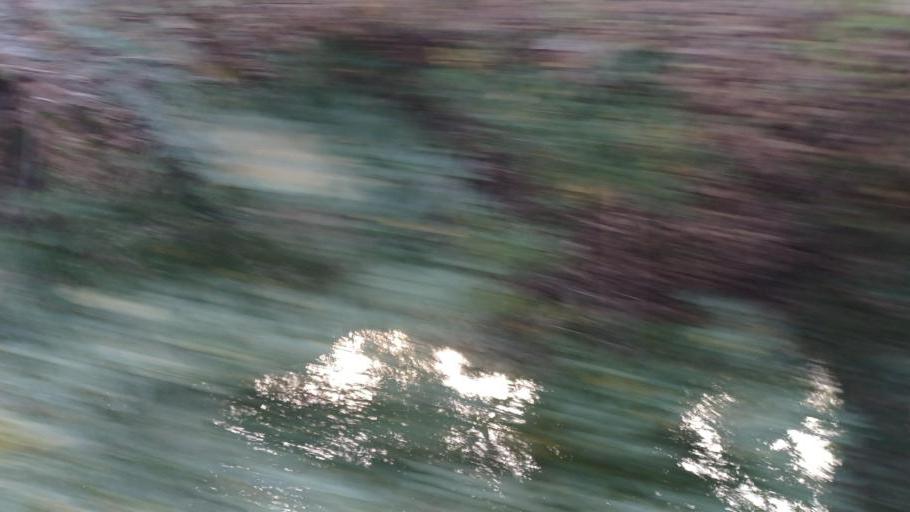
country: CY
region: Pafos
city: Polis
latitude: 34.9394
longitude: 32.5056
